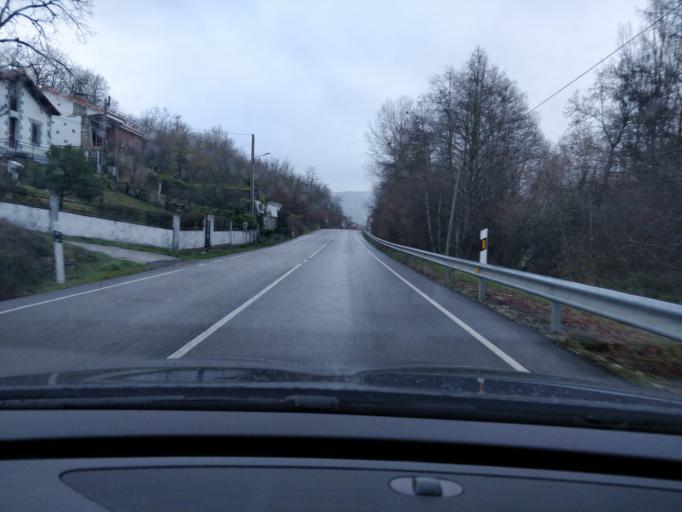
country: ES
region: Castille and Leon
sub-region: Provincia de Burgos
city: Espinosa de los Monteros
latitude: 43.0655
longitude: -3.5016
